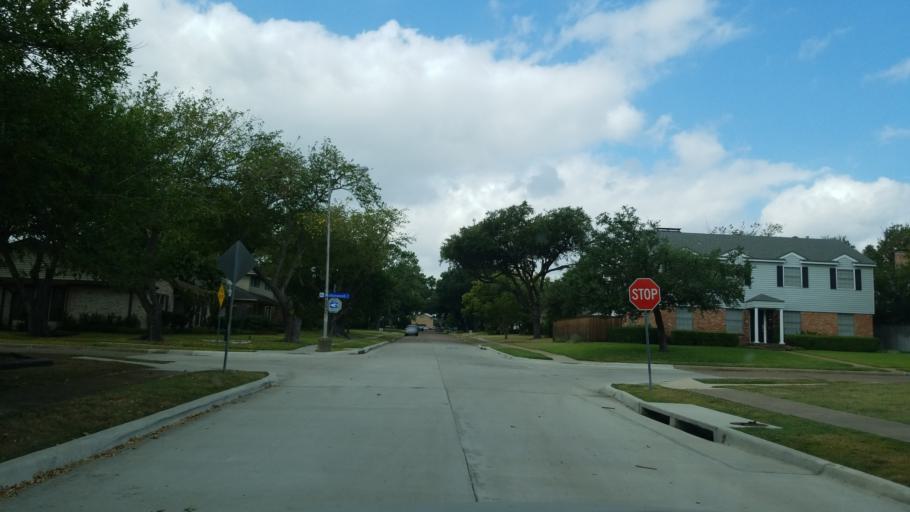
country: US
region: Texas
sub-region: Dallas County
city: Richardson
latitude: 32.9457
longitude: -96.7653
